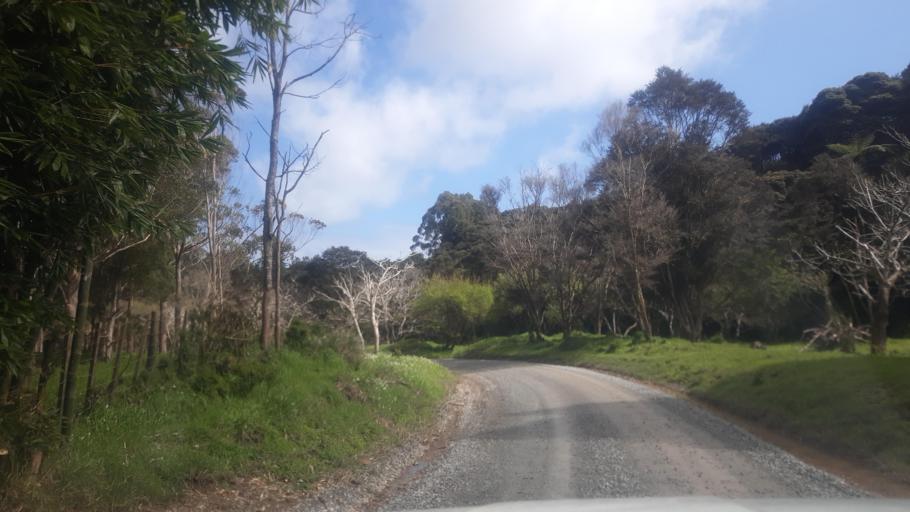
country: NZ
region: Northland
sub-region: Far North District
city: Taipa
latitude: -35.1130
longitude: 173.4304
